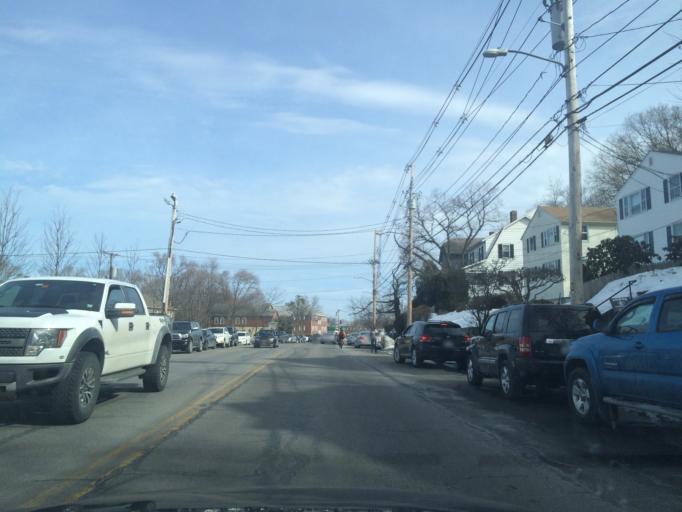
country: US
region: Massachusetts
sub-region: Middlesex County
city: Lexington
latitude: 42.4277
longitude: -71.2012
